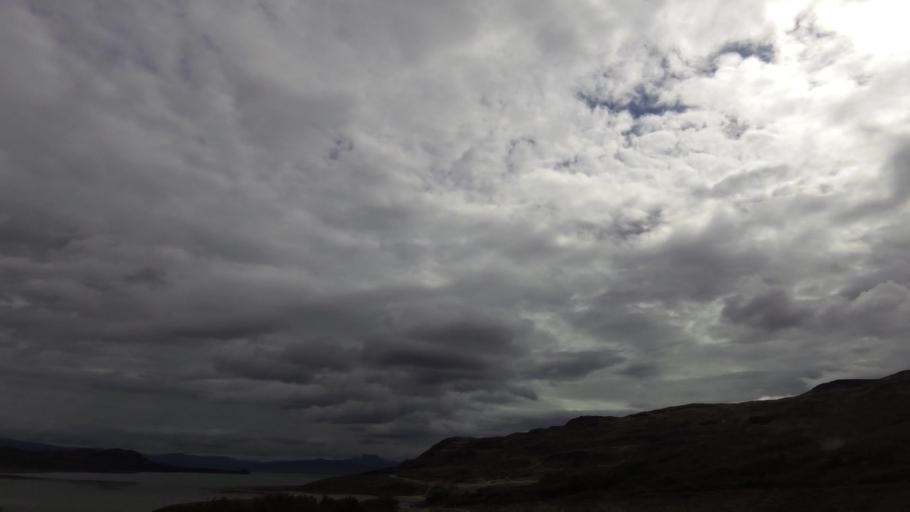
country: IS
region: West
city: Stykkisholmur
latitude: 65.5335
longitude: -22.1229
